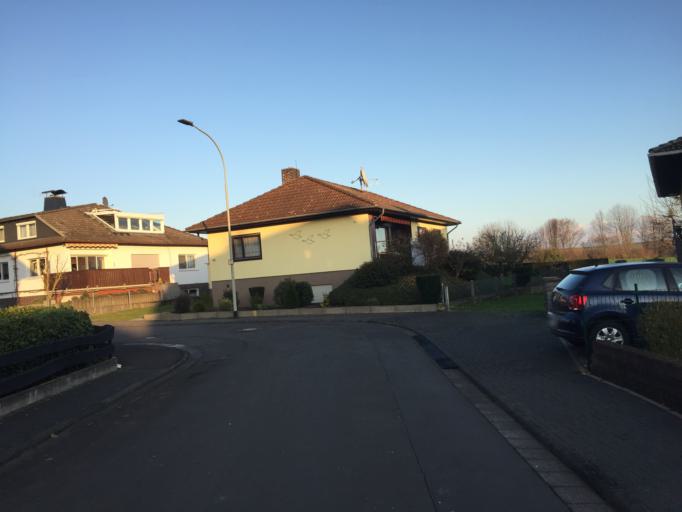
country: DE
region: Hesse
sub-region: Regierungsbezirk Darmstadt
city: Munzenberg
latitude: 50.4800
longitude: 8.7630
